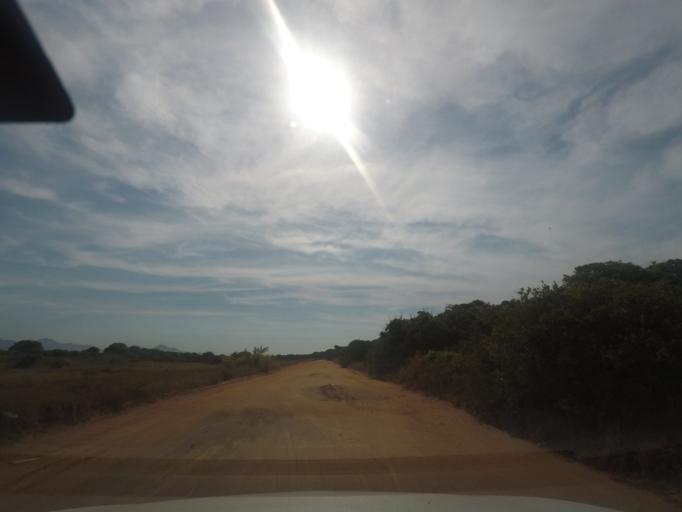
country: BR
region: Rio de Janeiro
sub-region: Marica
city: Marica
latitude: -22.9602
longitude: -42.8626
